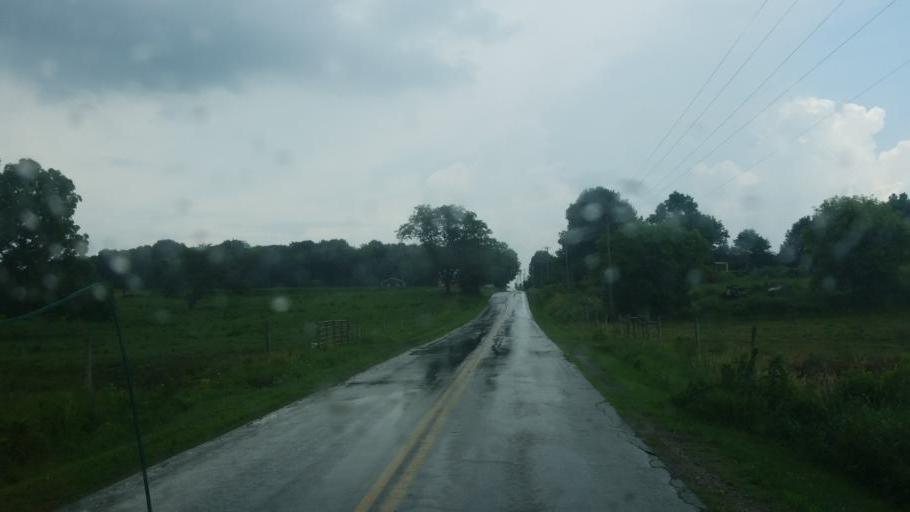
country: US
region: Ohio
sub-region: Wayne County
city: Smithville
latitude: 40.9018
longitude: -81.8152
